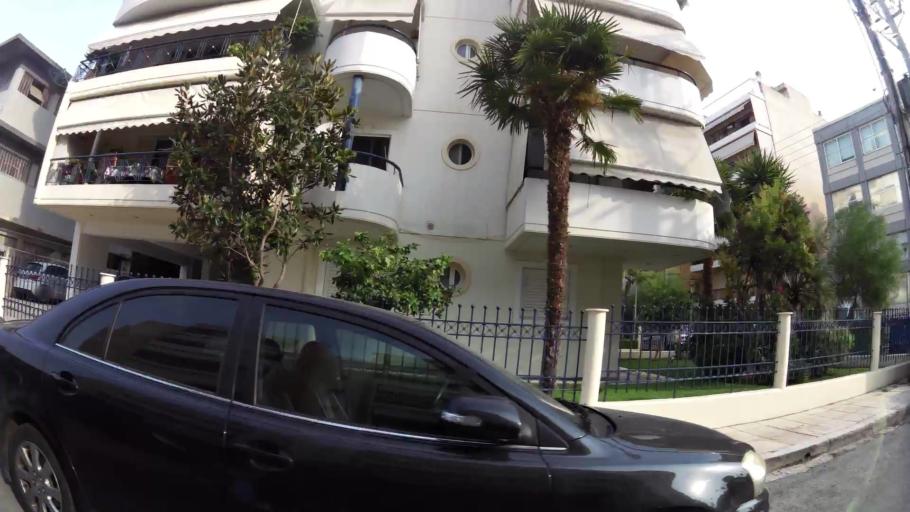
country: GR
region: Attica
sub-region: Nomarchia Athinas
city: Kallithea
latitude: 37.9548
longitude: 23.6888
